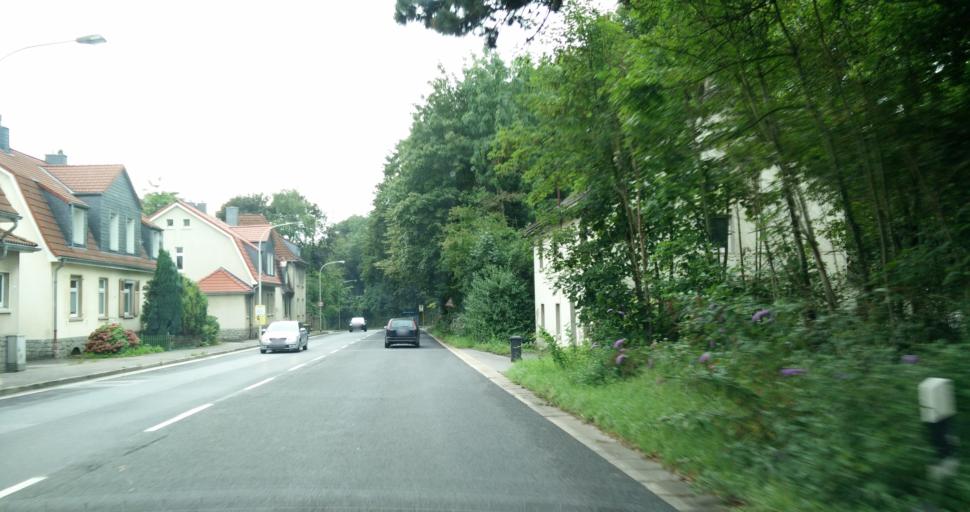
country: DE
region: North Rhine-Westphalia
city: Wulfrath
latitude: 51.2528
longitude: 7.0688
